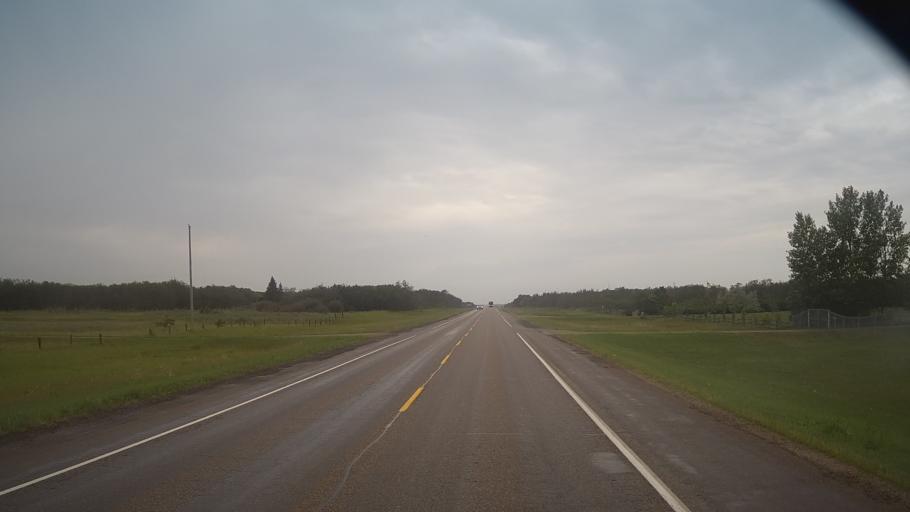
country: CA
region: Saskatchewan
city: Langham
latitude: 52.1294
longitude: -107.0365
